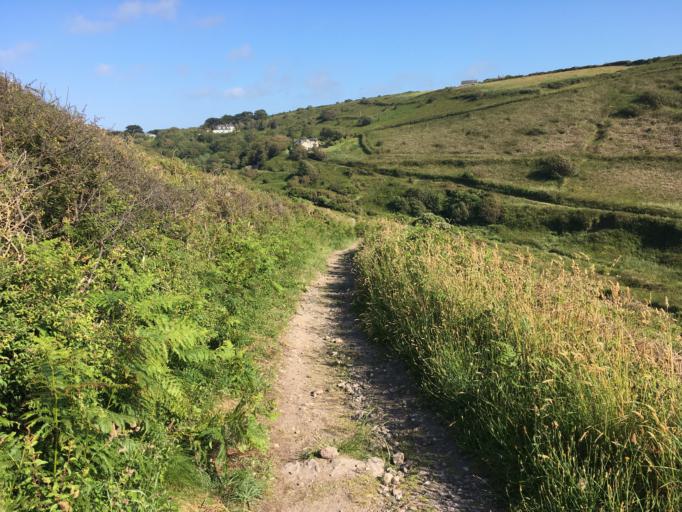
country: GB
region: England
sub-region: Cornwall
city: Saint Just
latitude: 50.1188
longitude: -5.6954
